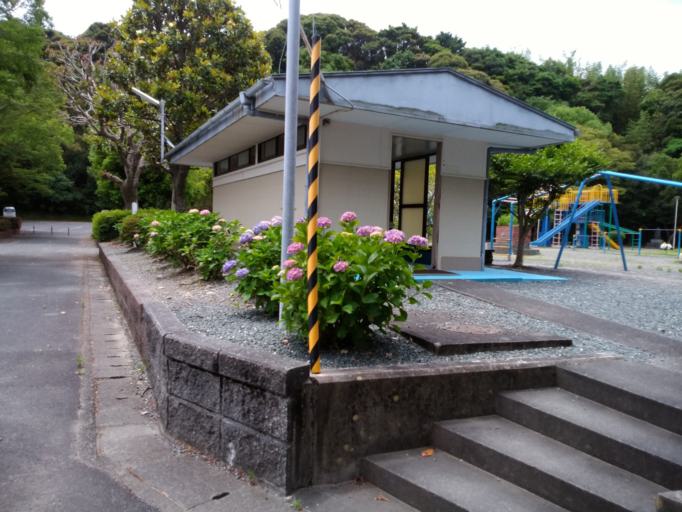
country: JP
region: Shizuoka
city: Kakegawa
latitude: 34.6949
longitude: 138.0718
